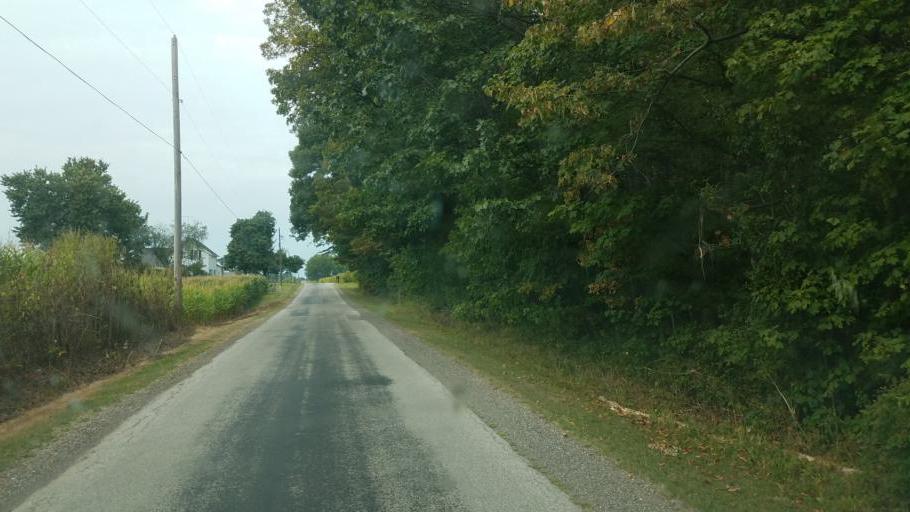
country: US
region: Ohio
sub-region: Marion County
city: Marion
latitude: 40.5132
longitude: -83.1022
